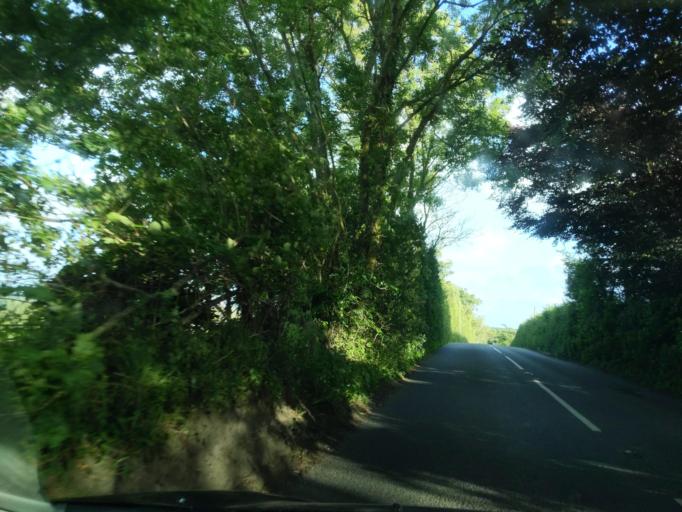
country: GB
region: England
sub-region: Devon
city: Fremington
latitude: 51.0548
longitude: -4.0899
